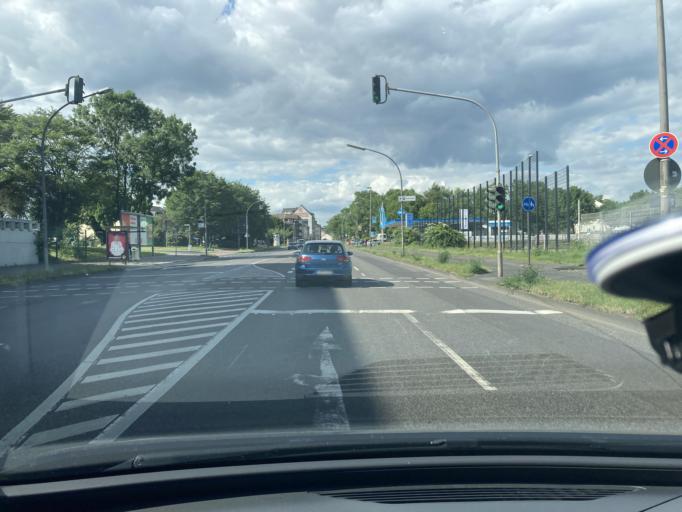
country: DE
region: North Rhine-Westphalia
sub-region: Regierungsbezirk Koln
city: Humboldtkolonie
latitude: 50.9259
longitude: 6.9998
